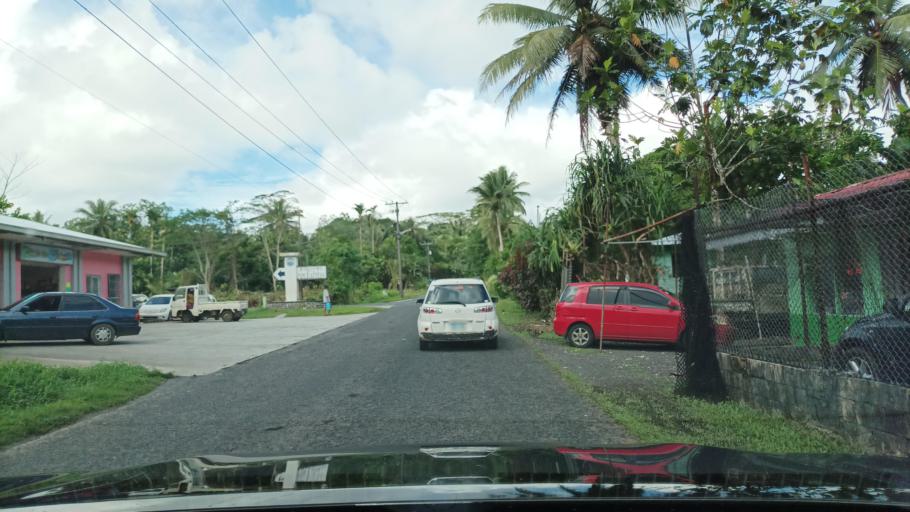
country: FM
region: Pohnpei
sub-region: Sokehs Municipality
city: Palikir - National Government Center
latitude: 6.9227
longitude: 158.1671
